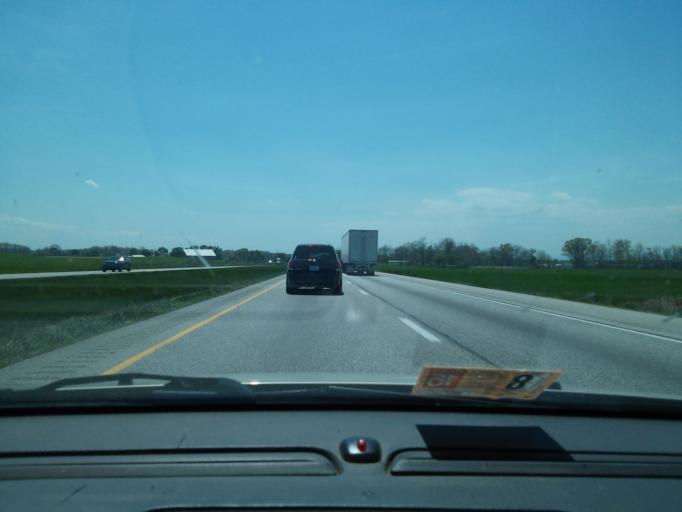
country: US
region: Pennsylvania
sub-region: Franklin County
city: Chambersburg
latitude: 39.8824
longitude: -77.6745
